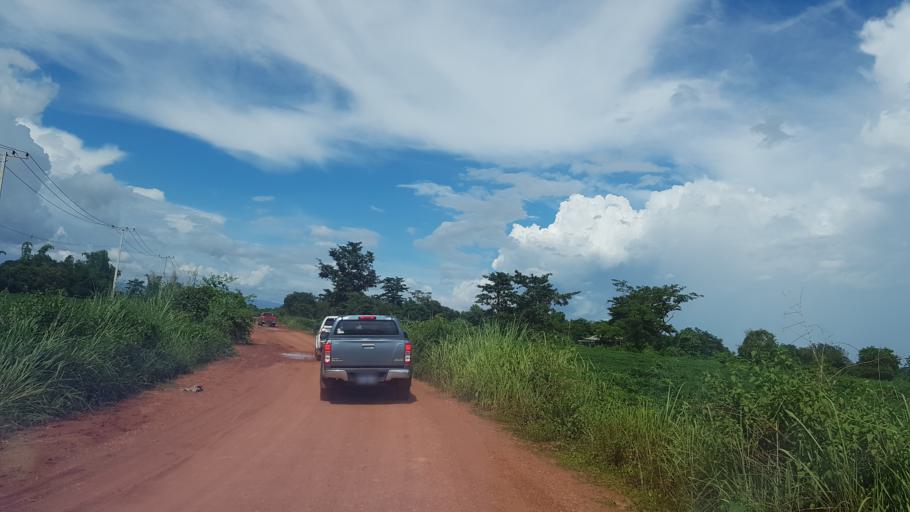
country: LA
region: Vientiane
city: Vientiane
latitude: 18.2050
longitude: 102.5688
